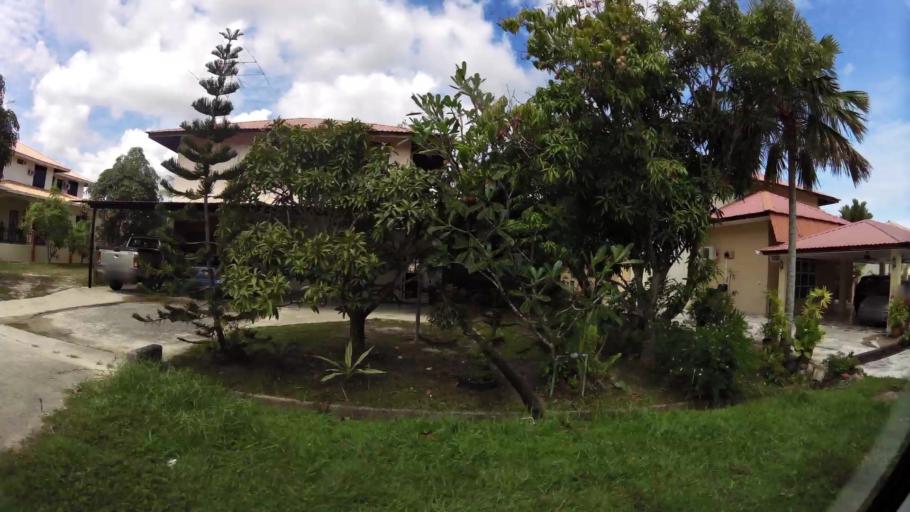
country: BN
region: Brunei and Muara
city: Bandar Seri Begawan
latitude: 4.9363
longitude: 114.8947
